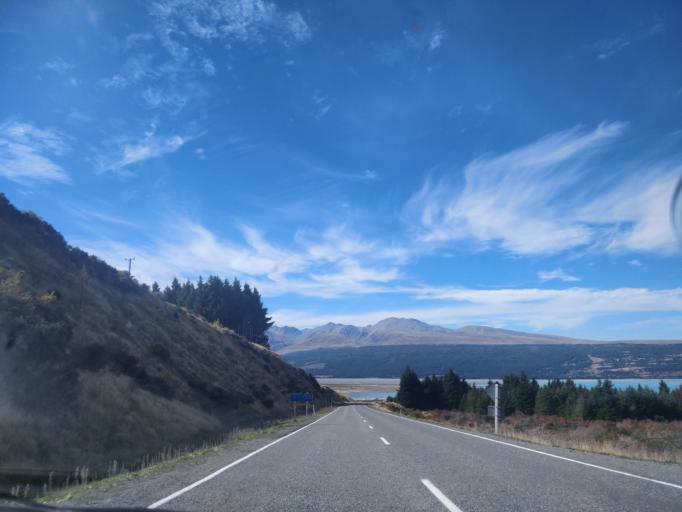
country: NZ
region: Canterbury
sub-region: Timaru District
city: Pleasant Point
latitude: -43.9147
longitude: 170.1152
